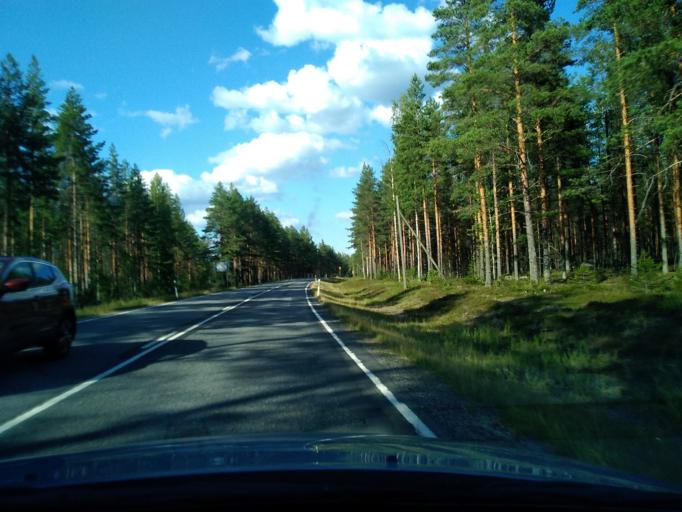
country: FI
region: Pirkanmaa
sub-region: Ylae-Pirkanmaa
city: Vilppula
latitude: 61.9460
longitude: 24.5421
